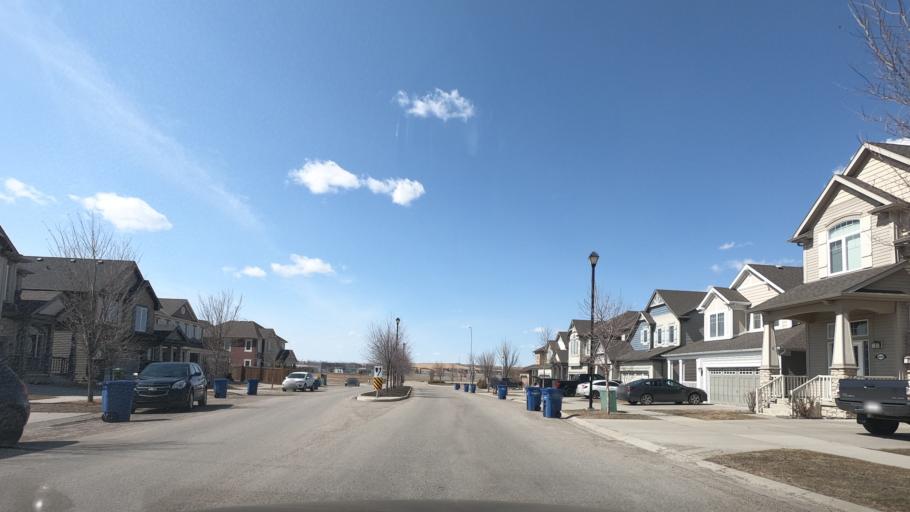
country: CA
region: Alberta
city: Airdrie
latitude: 51.2633
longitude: -114.0315
